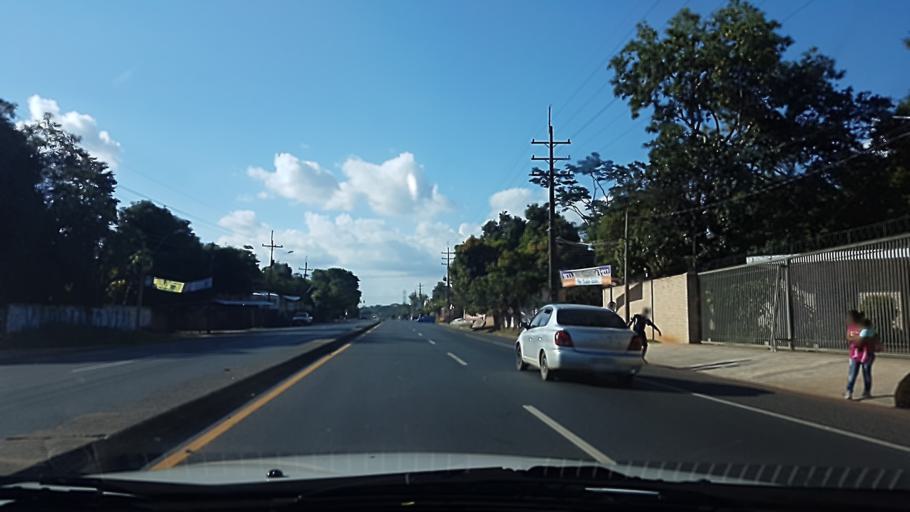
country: PY
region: Central
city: San Antonio
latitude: -25.4307
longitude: -57.5371
